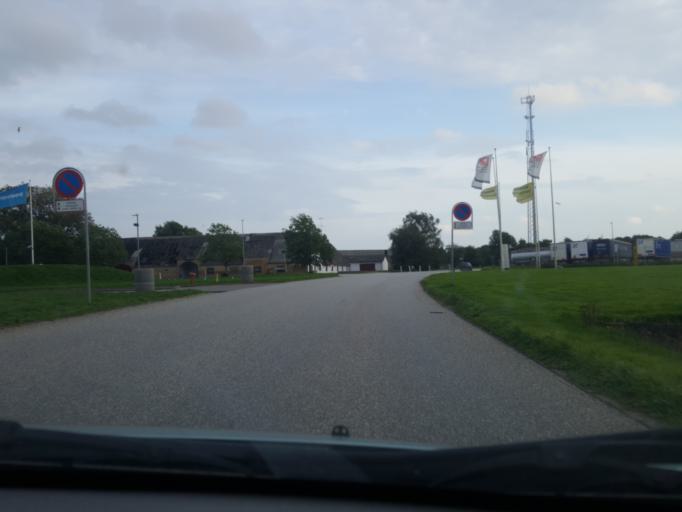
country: DK
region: South Denmark
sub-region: Fredericia Kommune
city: Taulov
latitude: 55.5422
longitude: 9.6292
